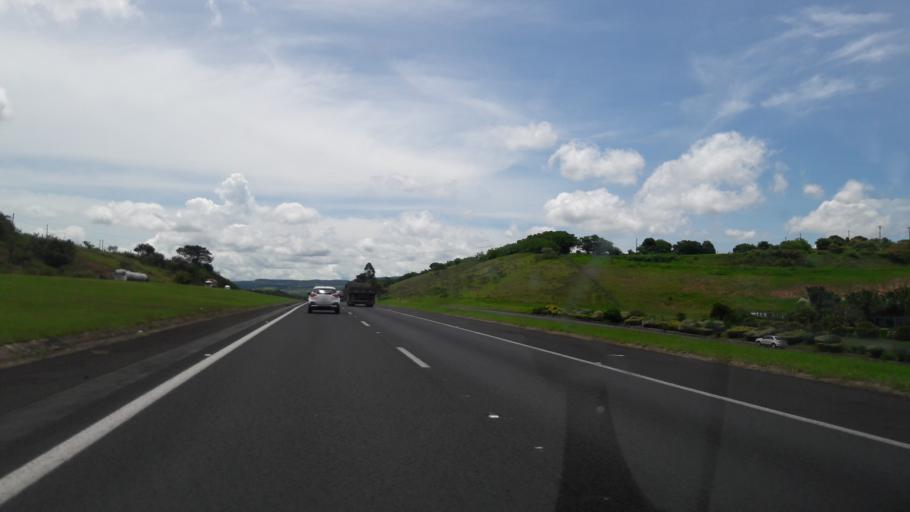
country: BR
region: Sao Paulo
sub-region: Itatinga
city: Itatinga
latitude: -23.1370
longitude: -48.4464
